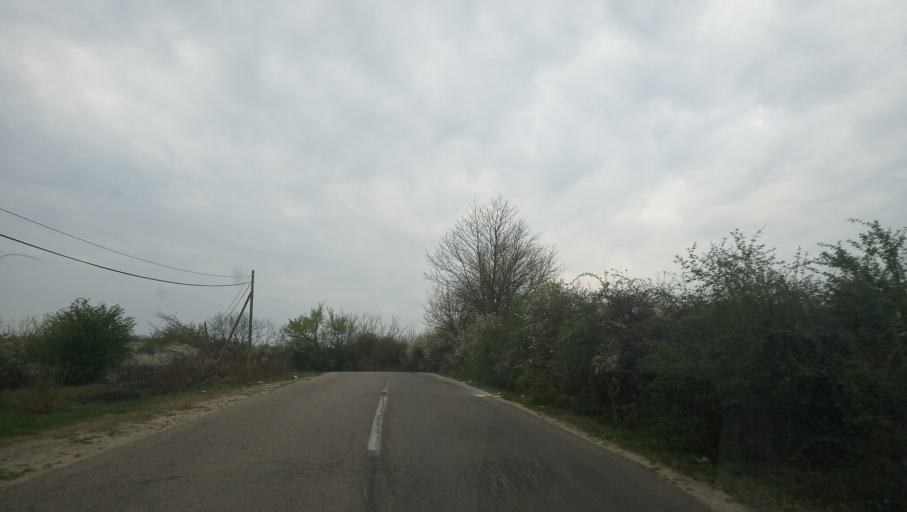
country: RO
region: Bihor
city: Hidiselu de Sus
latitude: 46.9238
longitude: 22.0514
